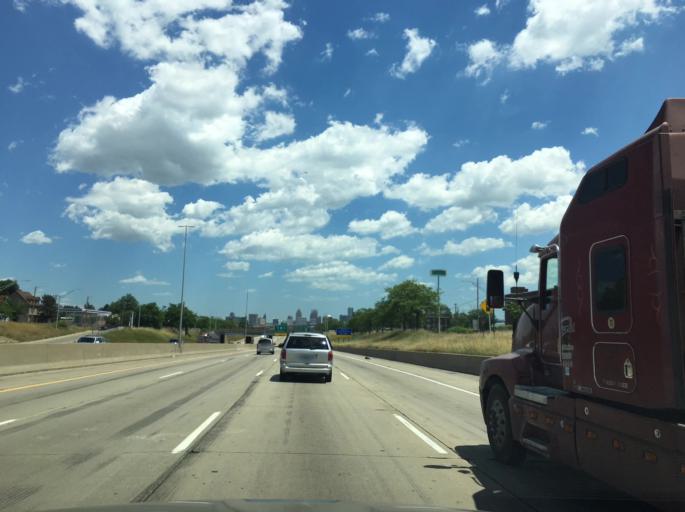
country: US
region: Michigan
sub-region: Wayne County
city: Detroit
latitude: 42.3124
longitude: -83.0939
